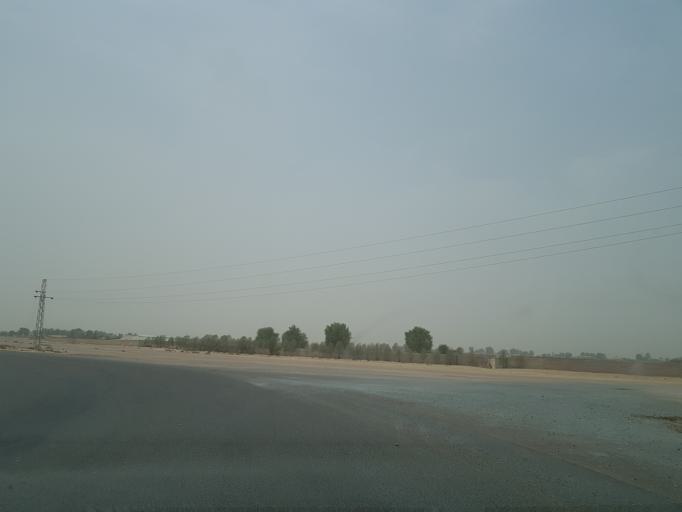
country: AE
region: Dubai
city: Dubai
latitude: 24.9416
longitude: 55.4799
